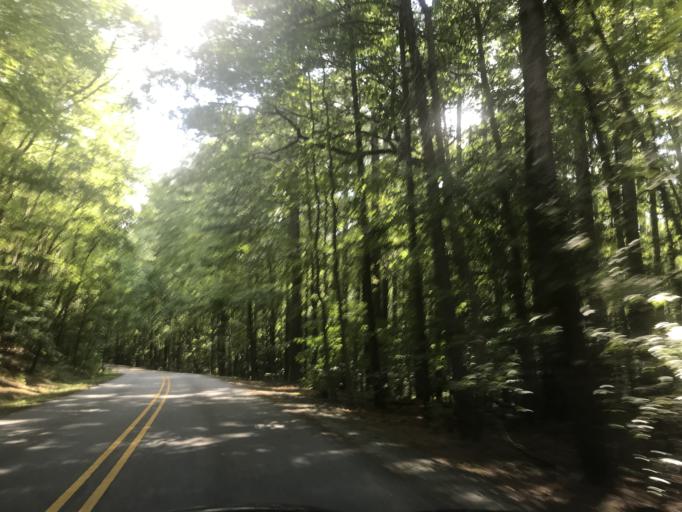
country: US
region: North Carolina
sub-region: Wake County
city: Morrisville
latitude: 35.8873
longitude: -78.7564
